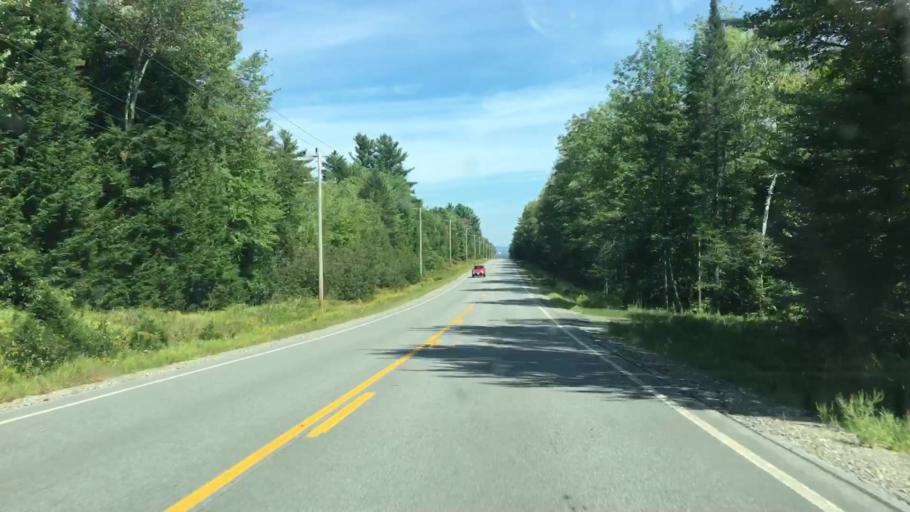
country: US
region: Maine
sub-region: Penobscot County
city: Howland
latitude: 45.2312
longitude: -68.7663
